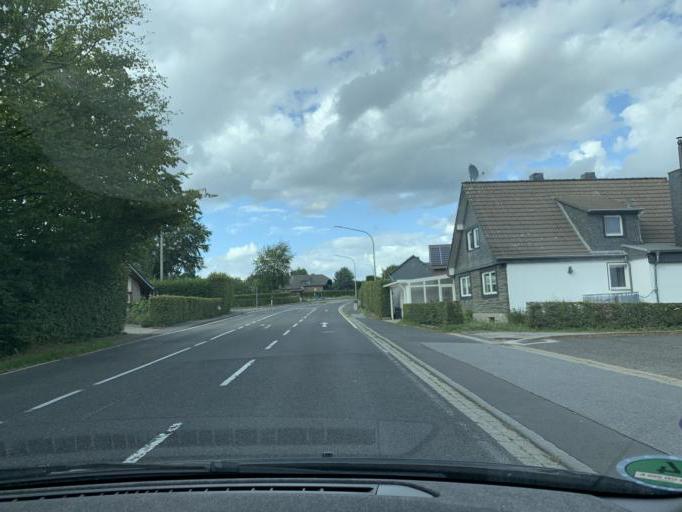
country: DE
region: North Rhine-Westphalia
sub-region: Regierungsbezirk Koln
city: Simmerath
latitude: 50.6123
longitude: 6.3091
